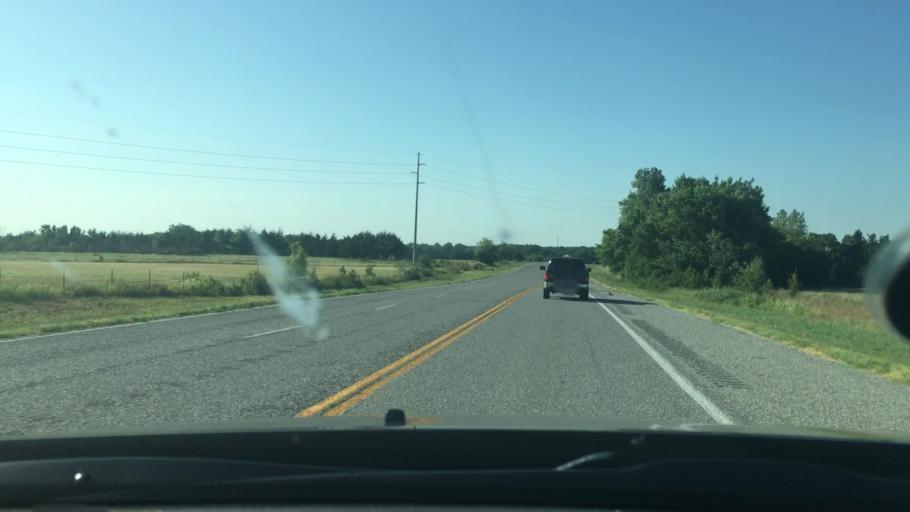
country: US
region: Oklahoma
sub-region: Johnston County
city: Tishomingo
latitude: 34.2758
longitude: -96.7772
